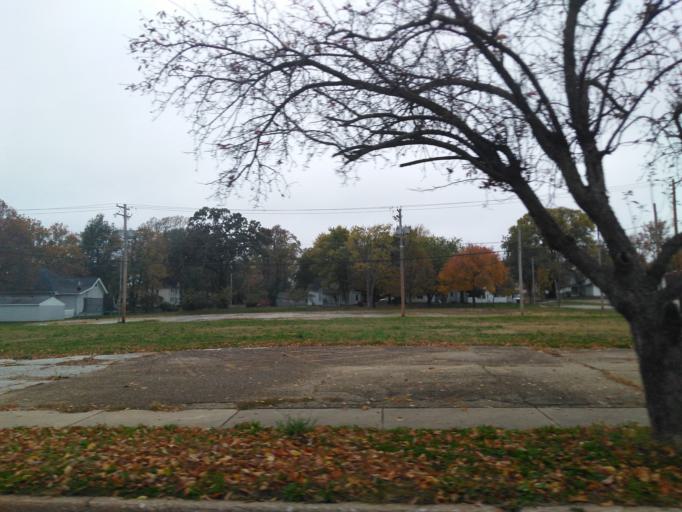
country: US
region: Illinois
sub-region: Bond County
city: Greenville
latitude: 38.8903
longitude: -89.4134
